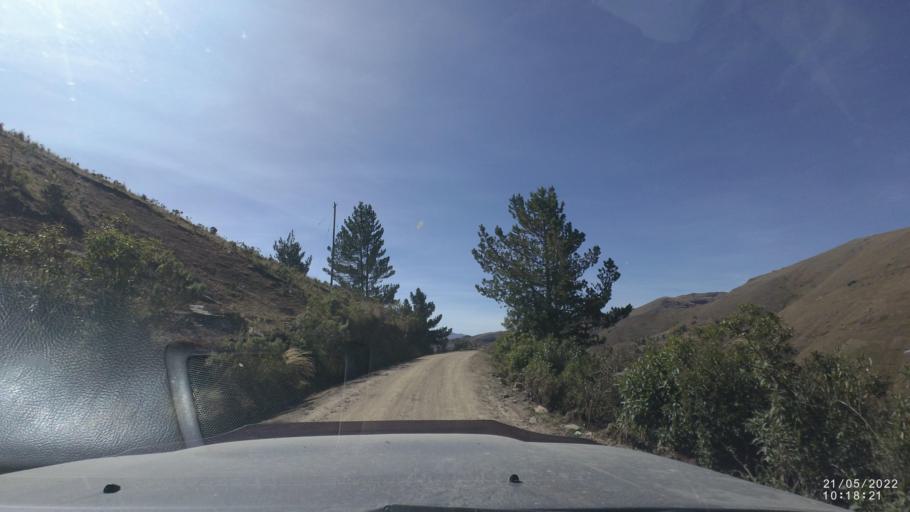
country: BO
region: Cochabamba
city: Colomi
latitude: -17.3275
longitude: -65.9614
